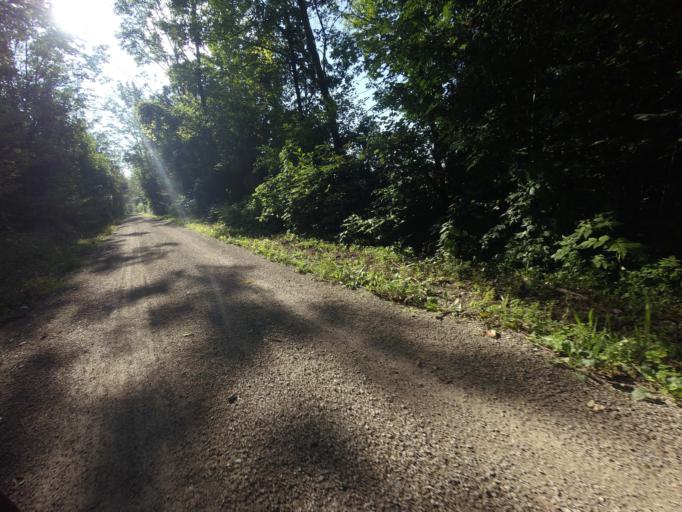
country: CA
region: Ontario
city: Huron East
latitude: 43.7387
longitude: -81.4667
